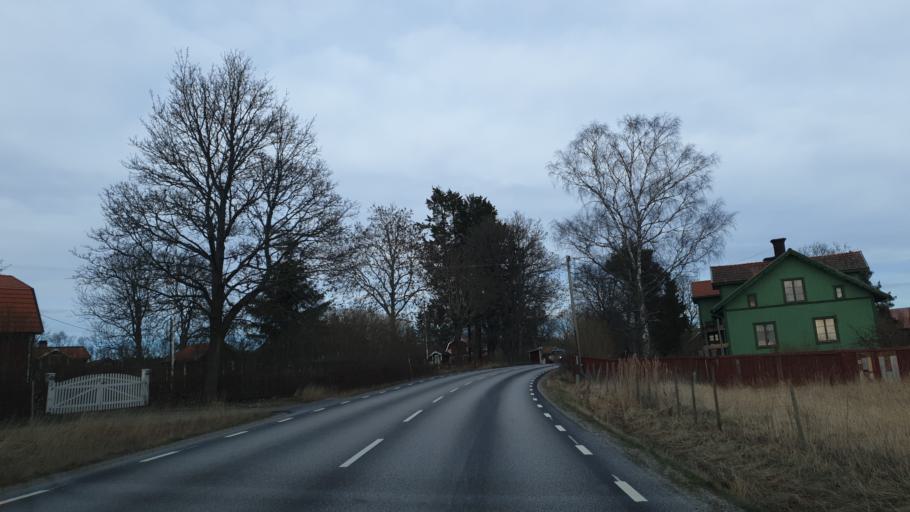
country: SE
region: Stockholm
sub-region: Osterakers Kommun
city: Akersberga
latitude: 59.5703
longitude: 18.2636
